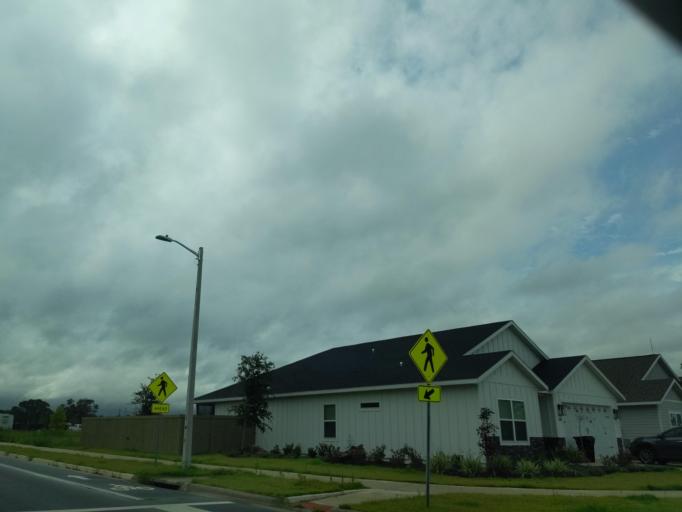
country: US
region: Florida
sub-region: Alachua County
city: Gainesville
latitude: 29.6377
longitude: -82.4192
